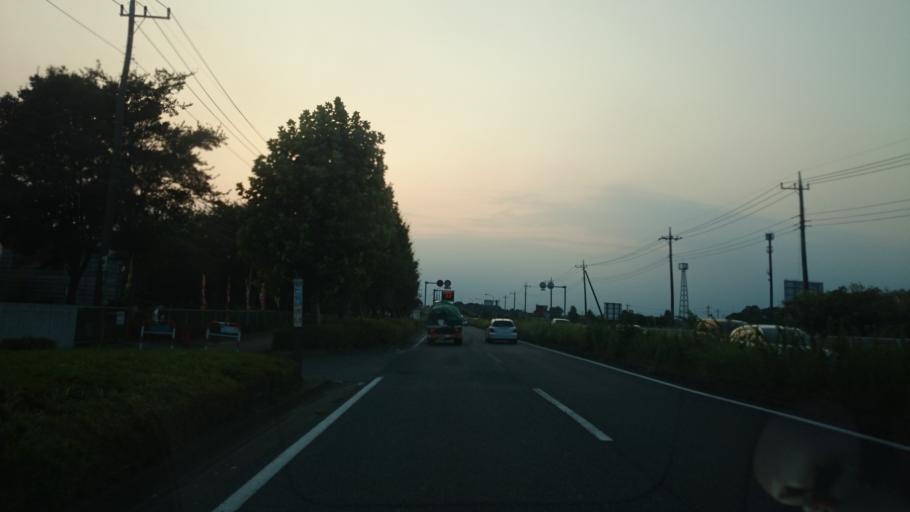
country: JP
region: Saitama
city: Hasuda
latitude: 35.9613
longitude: 139.6492
